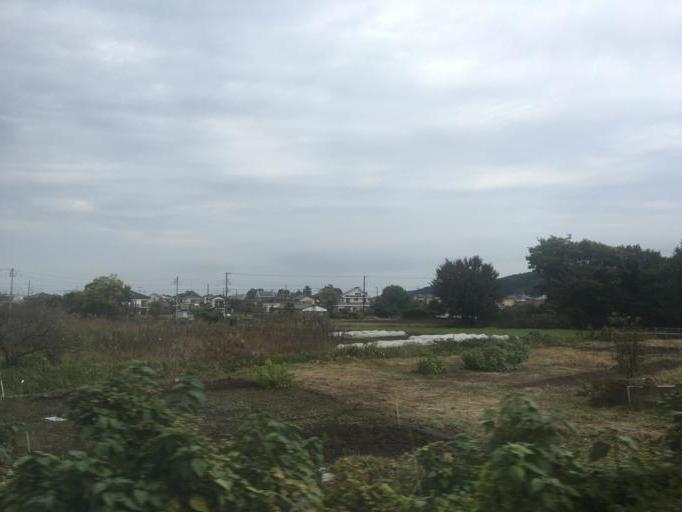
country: JP
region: Tokyo
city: Fussa
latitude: 35.7781
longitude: 139.3450
